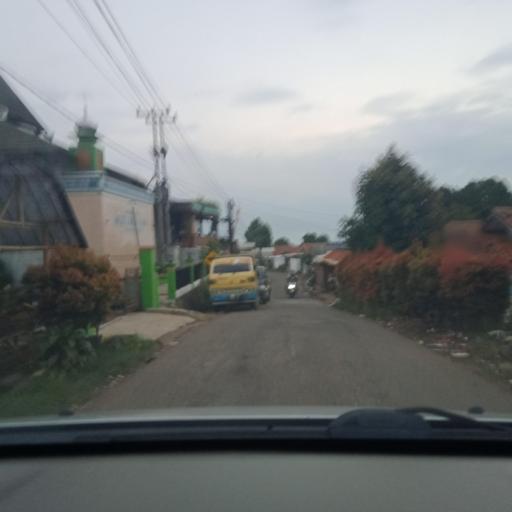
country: ID
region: West Java
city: Lembang
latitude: -6.8285
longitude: 107.5842
